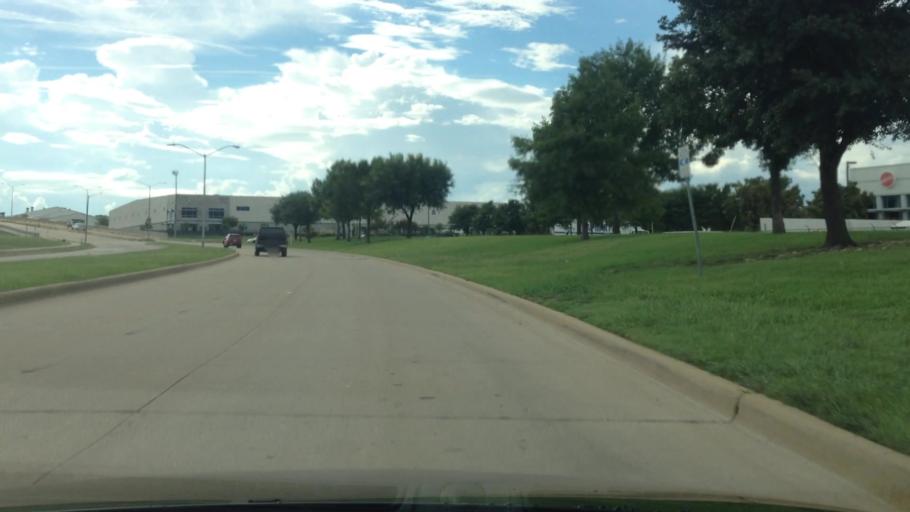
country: US
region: Texas
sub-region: Tarrant County
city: Blue Mound
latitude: 32.8266
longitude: -97.3505
